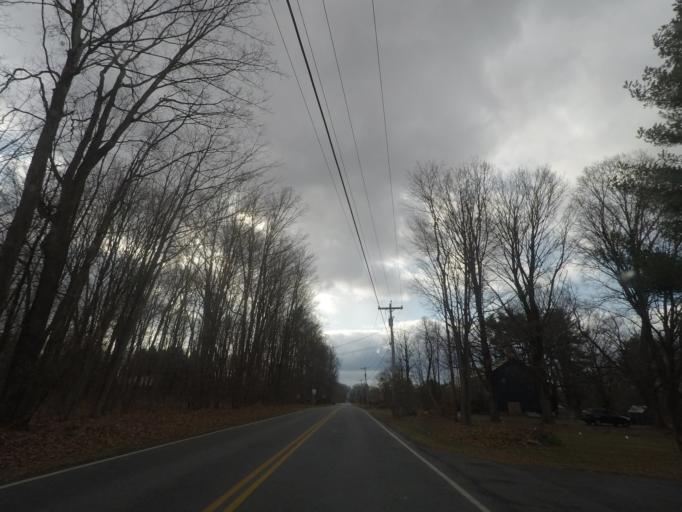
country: US
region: New York
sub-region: Saratoga County
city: Ballston Spa
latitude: 42.9947
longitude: -73.8146
